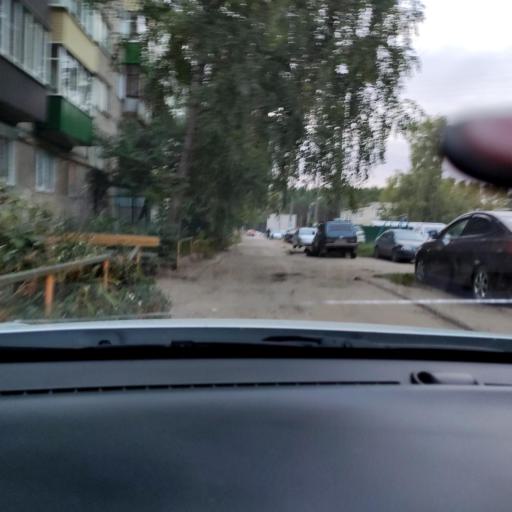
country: RU
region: Mariy-El
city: Volzhsk
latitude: 55.8661
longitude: 48.3458
